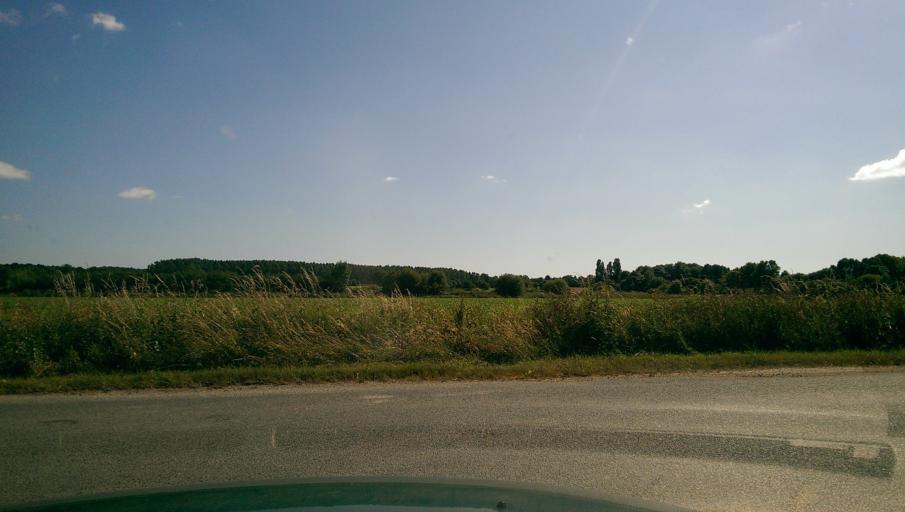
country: FR
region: Pays de la Loire
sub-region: Departement de la Vendee
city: Falleron
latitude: 46.8784
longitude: -1.7087
